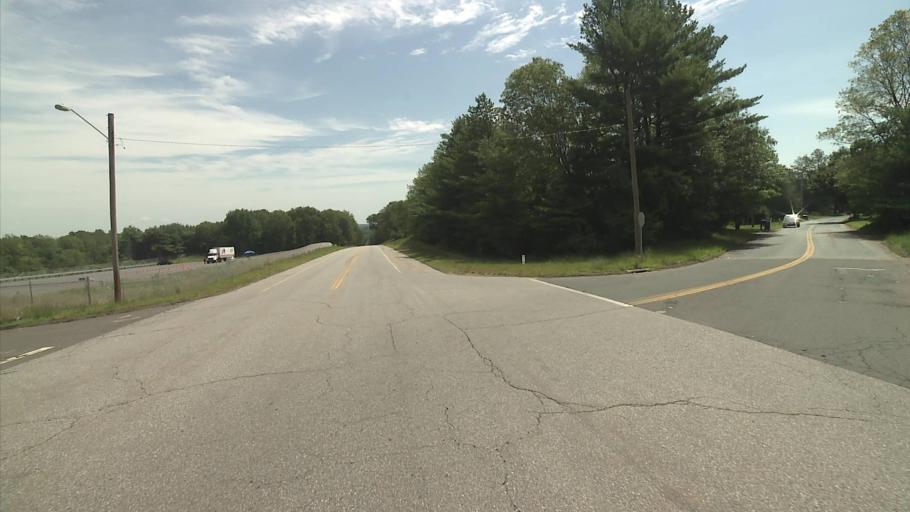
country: US
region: Connecticut
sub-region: Windham County
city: Willimantic
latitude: 41.7294
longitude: -72.2111
